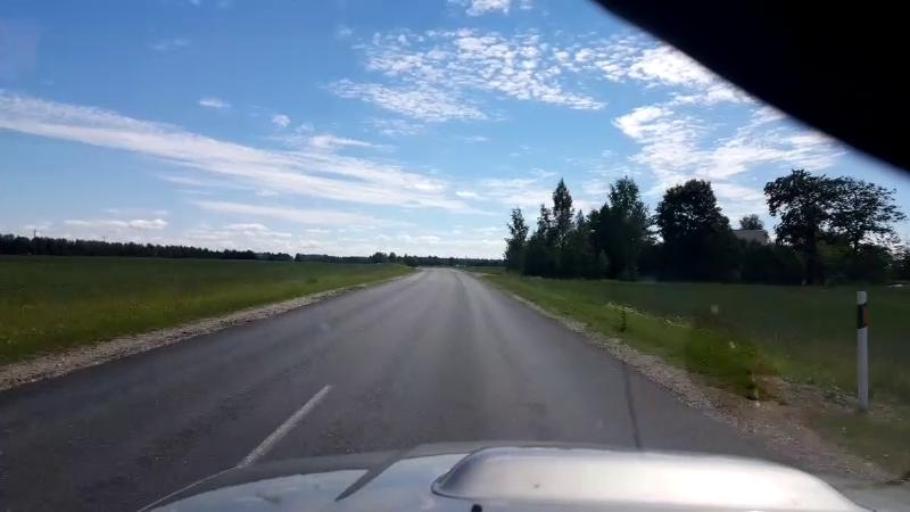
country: EE
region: Laeaene-Virumaa
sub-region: Rakke vald
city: Rakke
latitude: 58.8977
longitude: 26.2829
